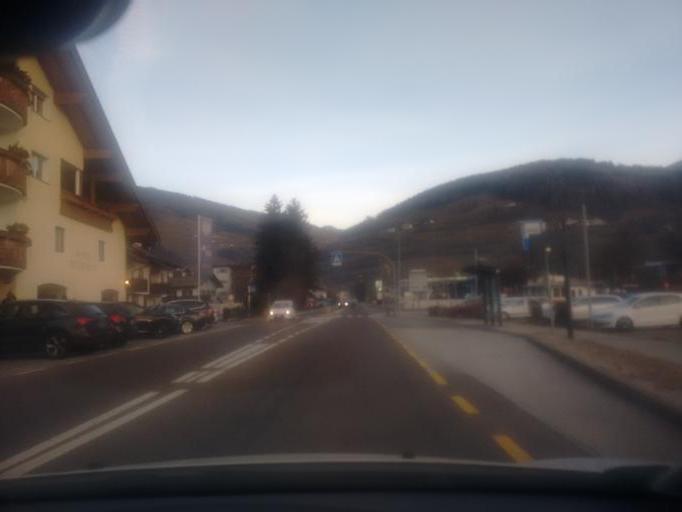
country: IT
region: Trentino-Alto Adige
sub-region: Bolzano
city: Vipiteno
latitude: 46.8928
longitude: 11.4357
